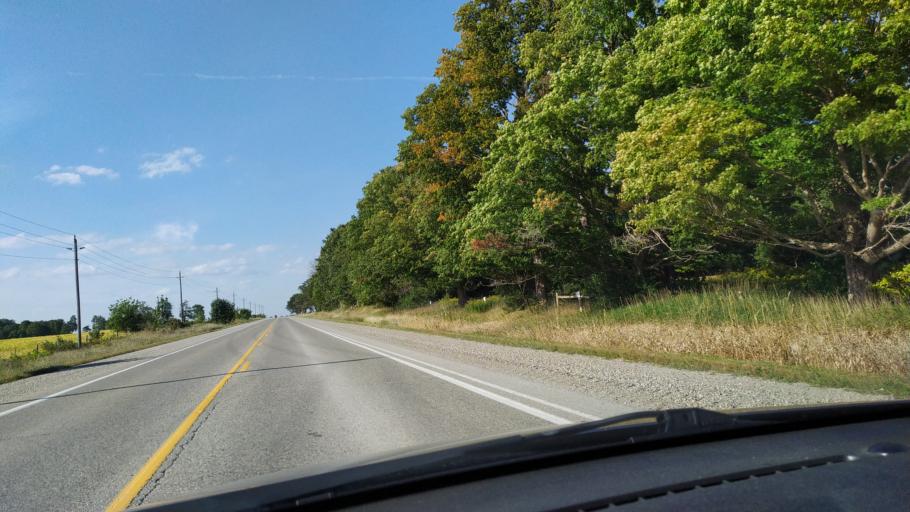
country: CA
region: Ontario
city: Ingersoll
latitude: 43.0808
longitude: -80.8624
